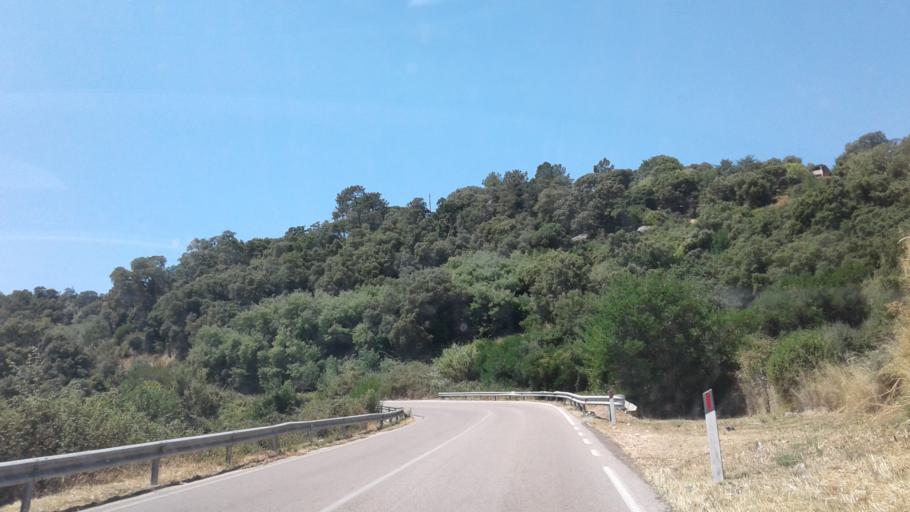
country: IT
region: Sardinia
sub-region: Provincia di Olbia-Tempio
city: Luras
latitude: 40.9333
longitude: 9.1833
